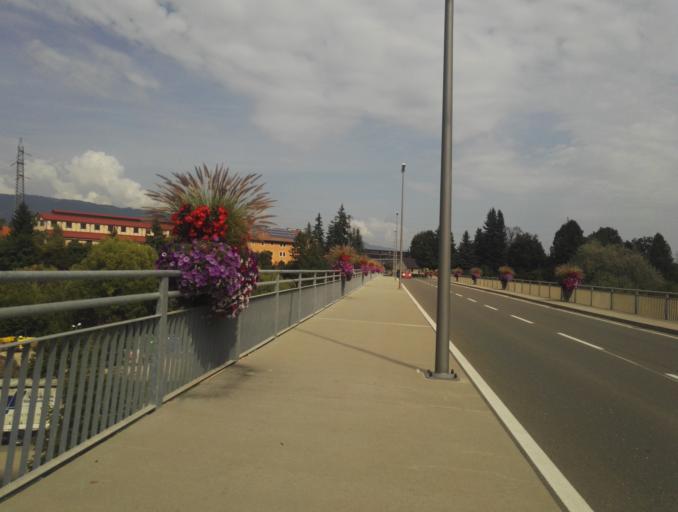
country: AT
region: Styria
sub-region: Politischer Bezirk Murtal
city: Judenburg
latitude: 47.1712
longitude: 14.6646
